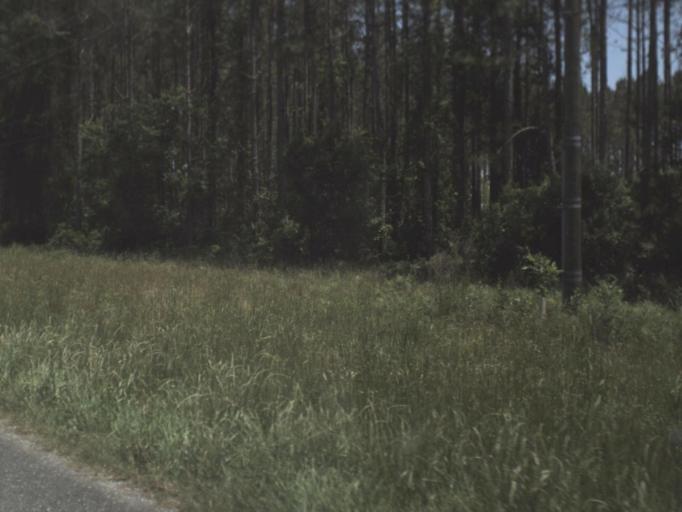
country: US
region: Florida
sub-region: Columbia County
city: Watertown
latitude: 30.1935
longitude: -82.5121
